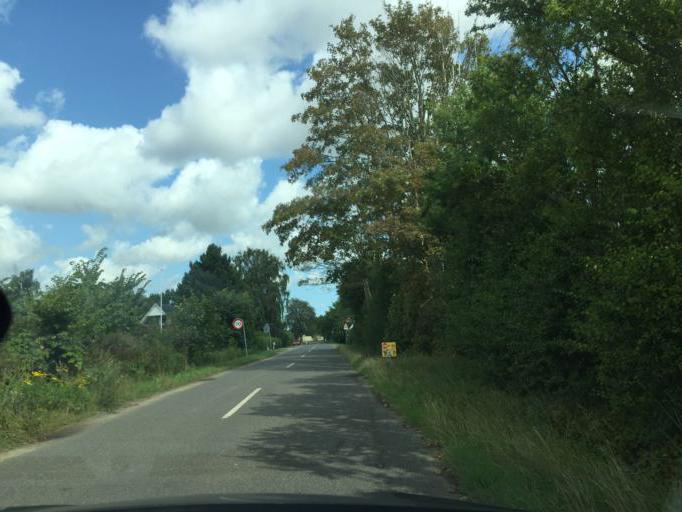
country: DK
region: South Denmark
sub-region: Odense Kommune
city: Stige
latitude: 55.4683
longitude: 10.3802
